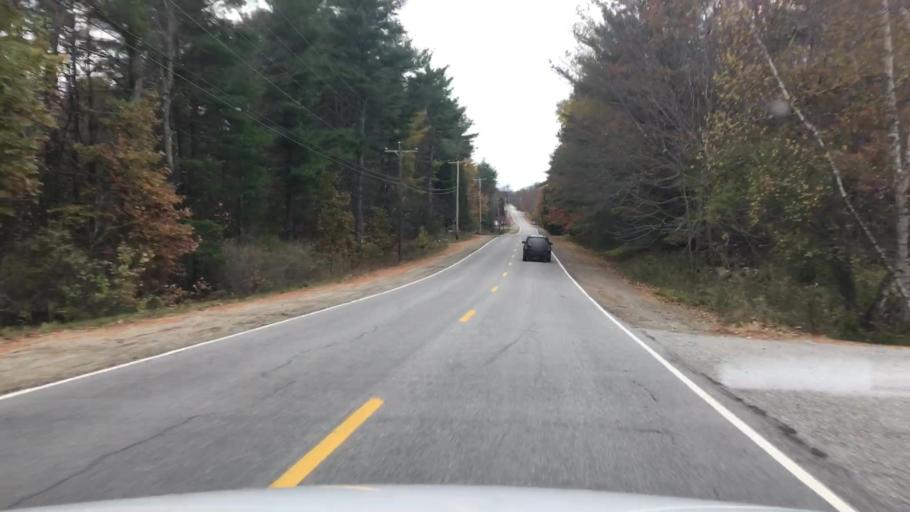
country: US
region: Maine
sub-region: Kennebec County
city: Monmouth
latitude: 44.1892
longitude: -70.0682
